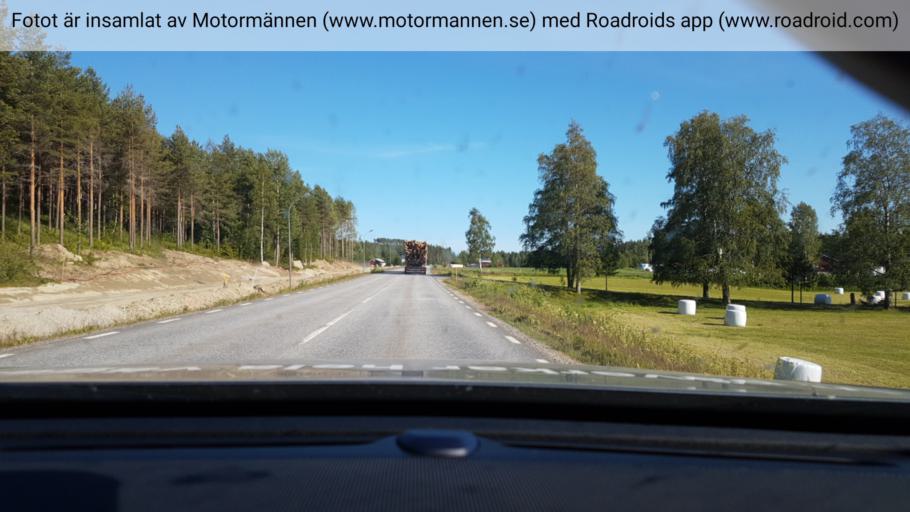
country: SE
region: Vaesterbotten
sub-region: Bjurholms Kommun
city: Bjurholm
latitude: 64.2386
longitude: 19.3390
